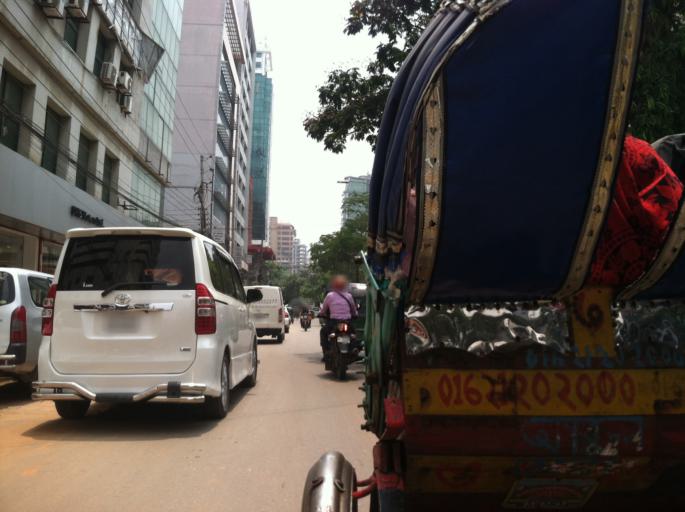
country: BD
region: Dhaka
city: Paltan
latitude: 23.7810
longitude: 90.4008
